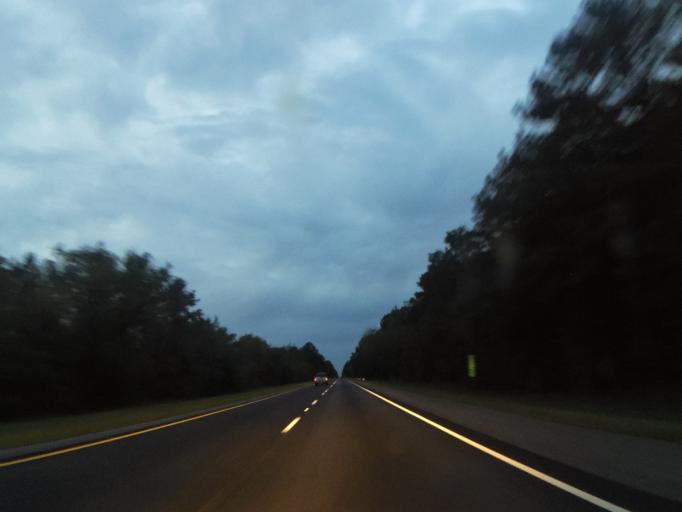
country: US
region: Alabama
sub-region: DeKalb County
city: Collinsville
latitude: 34.2254
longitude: -85.9194
